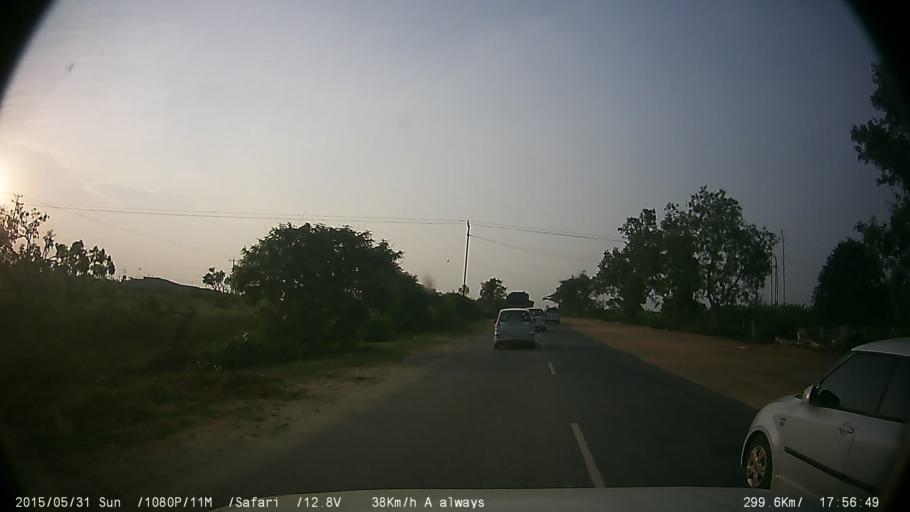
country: IN
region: Karnataka
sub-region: Mysore
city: Nanjangud
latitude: 11.9967
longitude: 76.6696
